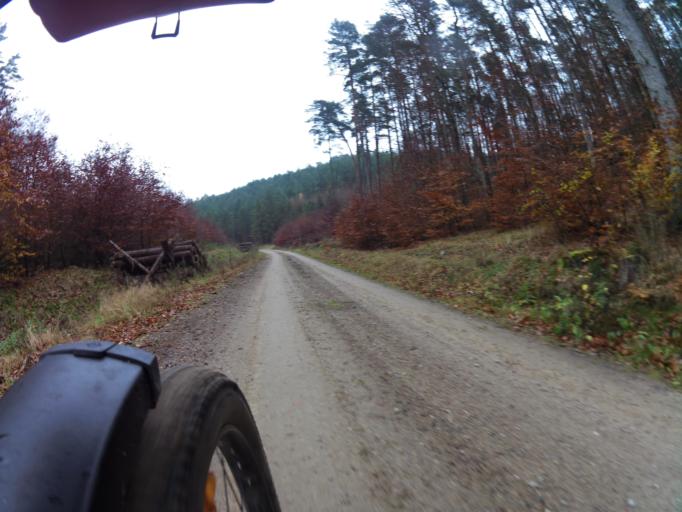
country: PL
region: Pomeranian Voivodeship
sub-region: Powiat wejherowski
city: Orle
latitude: 54.7074
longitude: 18.1464
